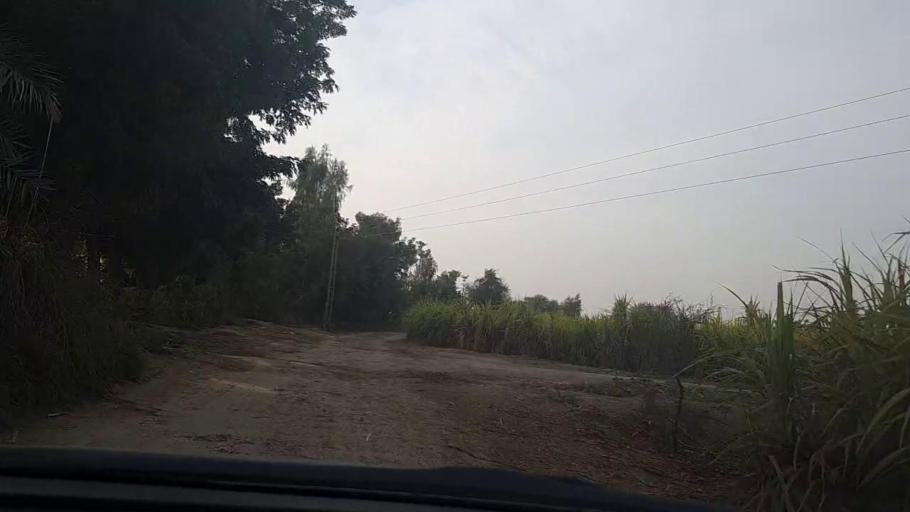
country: PK
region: Sindh
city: Daulatpur
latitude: 26.3349
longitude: 68.0395
